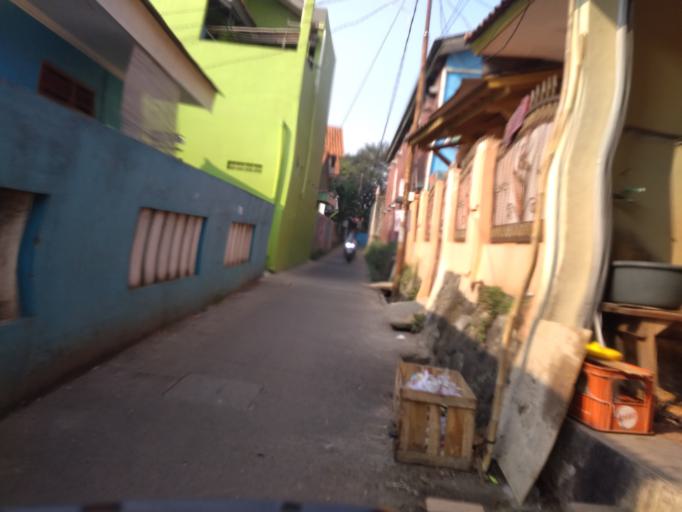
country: ID
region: West Java
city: Depok
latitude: -6.3567
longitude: 106.8414
